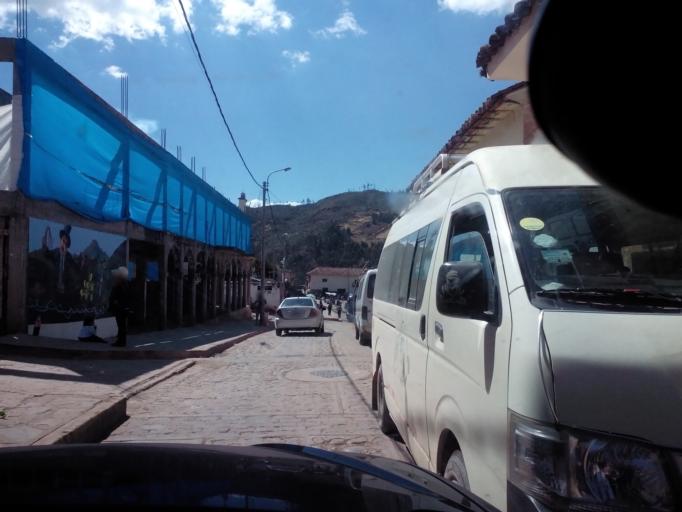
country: PE
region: Cusco
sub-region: Provincia de Anta
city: Huarocondo
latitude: -13.4160
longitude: -72.2083
